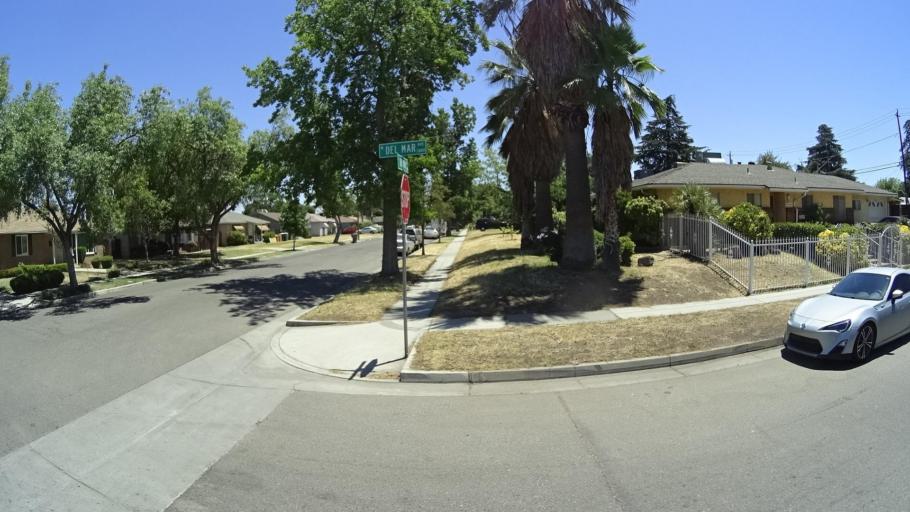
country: US
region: California
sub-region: Fresno County
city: Fresno
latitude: 36.7749
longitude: -119.7951
